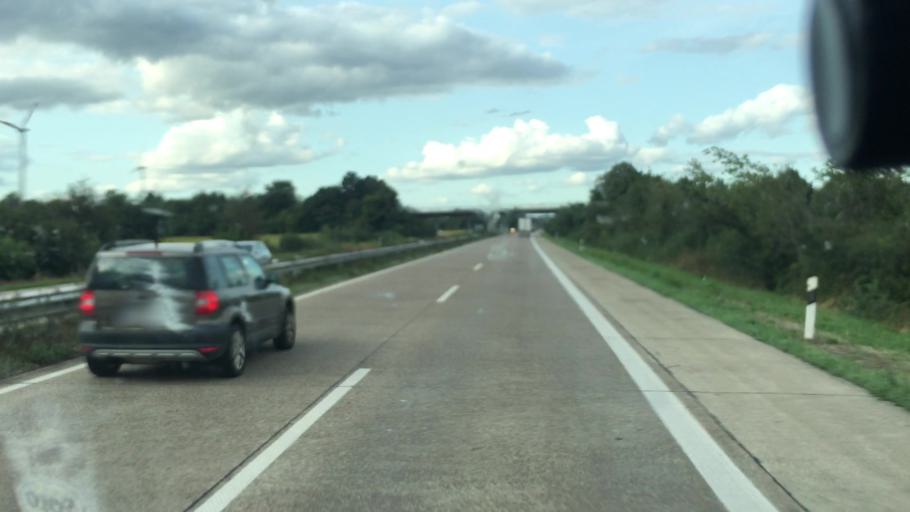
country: DE
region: Lower Saxony
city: Grossenkneten
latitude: 52.9605
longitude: 8.1826
